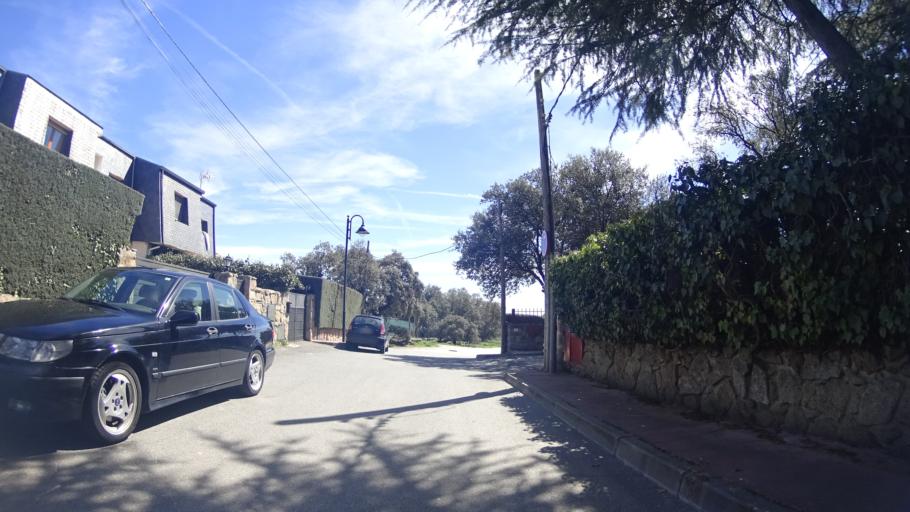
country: ES
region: Madrid
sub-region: Provincia de Madrid
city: Galapagar
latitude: 40.5904
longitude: -3.9850
